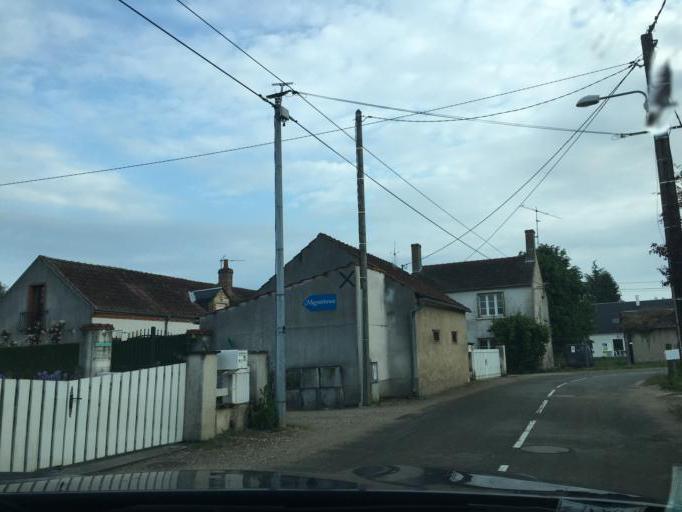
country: FR
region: Centre
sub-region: Departement du Loiret
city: Saint-Denis-en-Val
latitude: 47.8928
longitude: 1.9524
